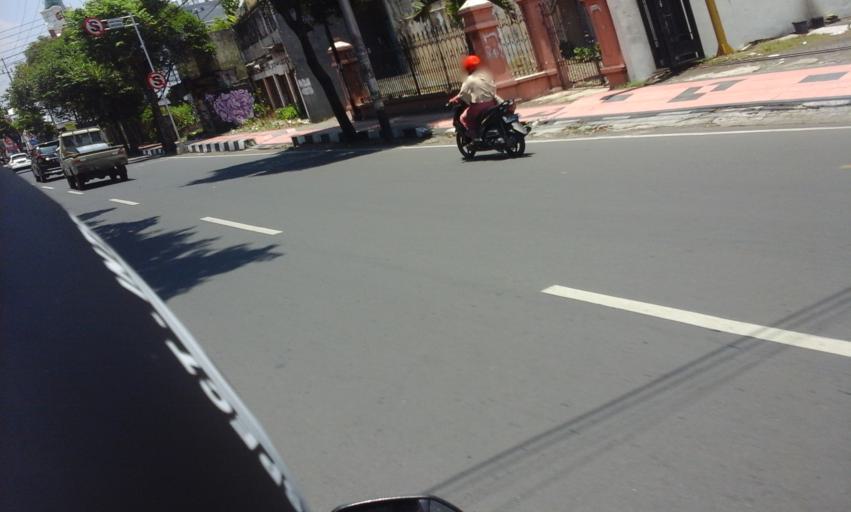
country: ID
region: East Java
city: Kepatihan
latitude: -8.1753
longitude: 113.7014
